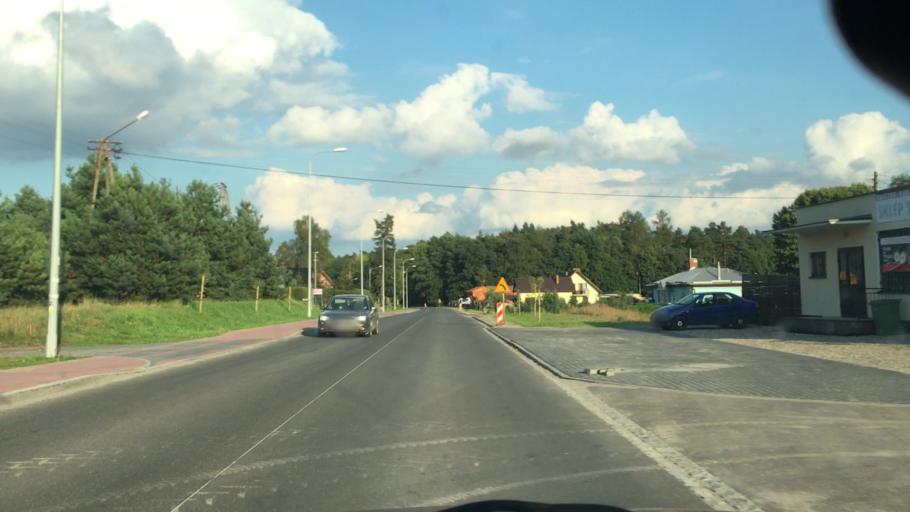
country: PL
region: Pomeranian Voivodeship
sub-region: Powiat starogardzki
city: Bobowo
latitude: 53.9272
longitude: 18.6080
